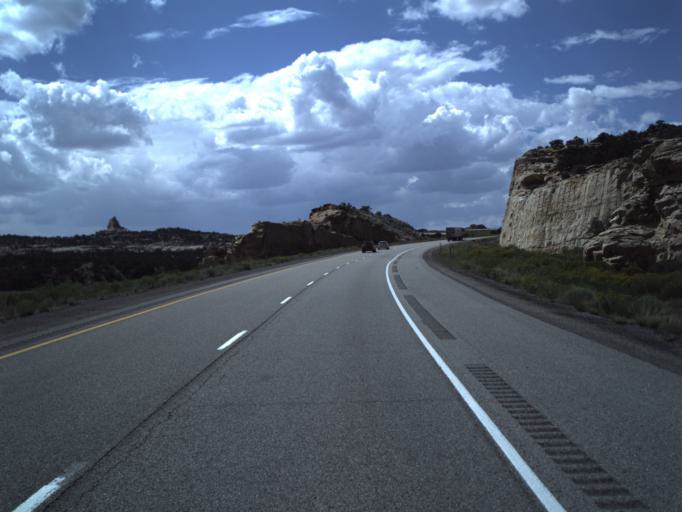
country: US
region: Utah
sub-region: Emery County
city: Ferron
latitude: 38.8652
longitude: -110.7947
